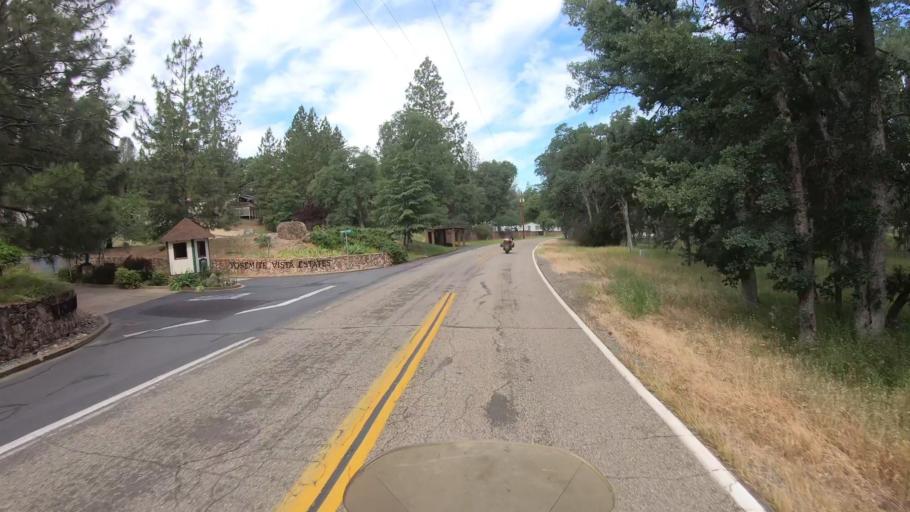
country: US
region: California
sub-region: Tuolumne County
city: Tuolumne City
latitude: 37.8459
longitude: -120.1387
